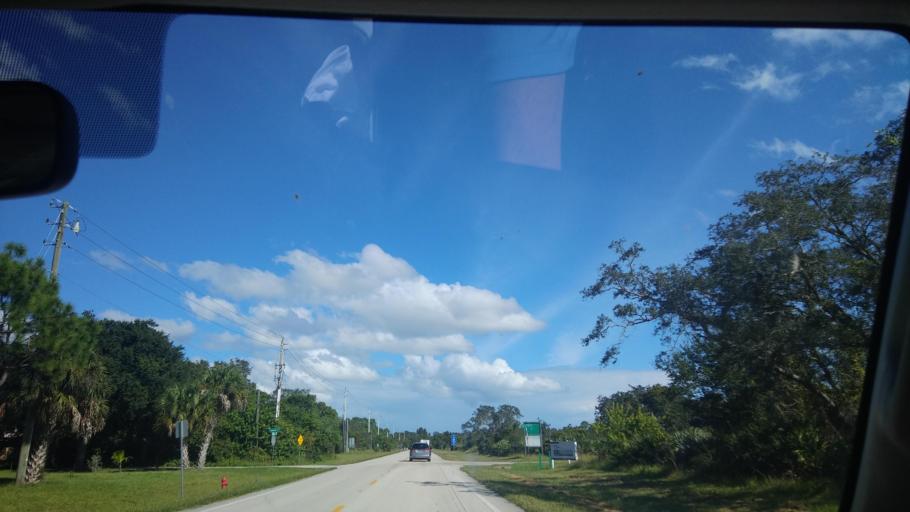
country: US
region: Florida
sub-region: Indian River County
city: Roseland
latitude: 27.8186
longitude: -80.5042
